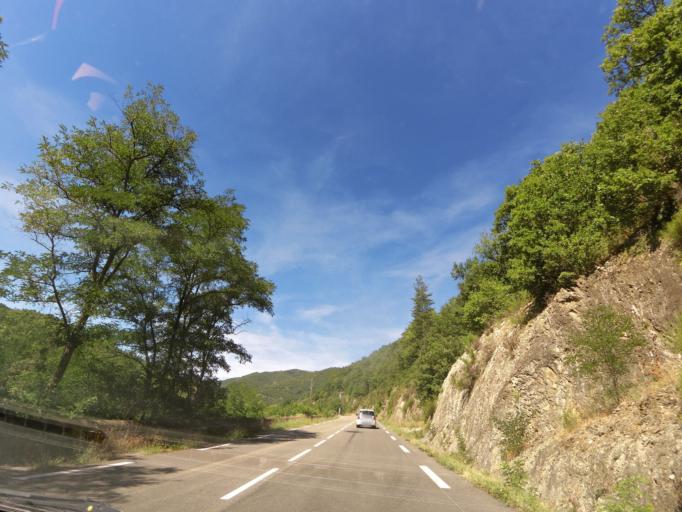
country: FR
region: Languedoc-Roussillon
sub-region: Departement du Gard
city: Le Vigan
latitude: 43.9781
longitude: 3.4902
